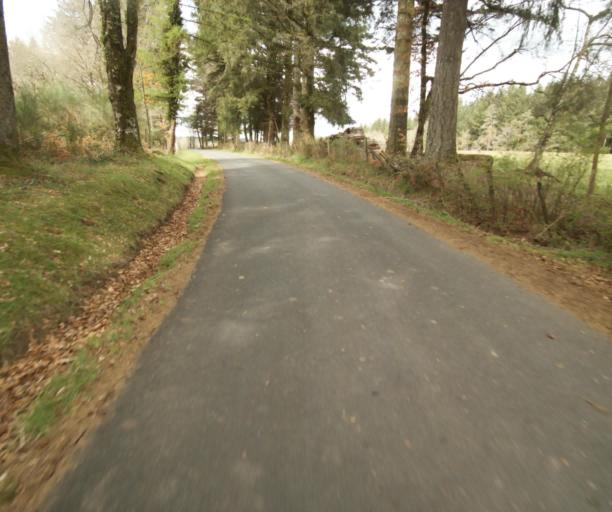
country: FR
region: Limousin
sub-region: Departement de la Correze
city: Correze
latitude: 45.3410
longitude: 1.9627
